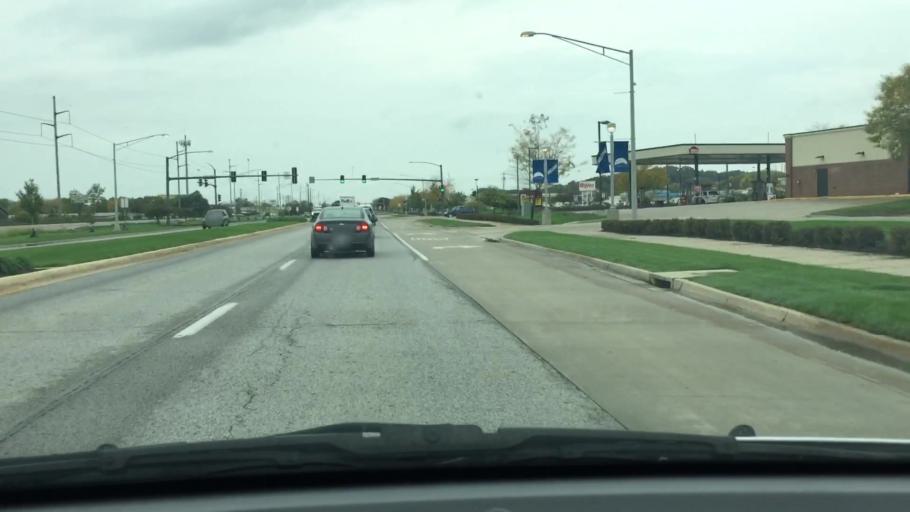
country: US
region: Iowa
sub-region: Johnson County
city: Coralville
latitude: 41.6789
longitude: -91.5903
